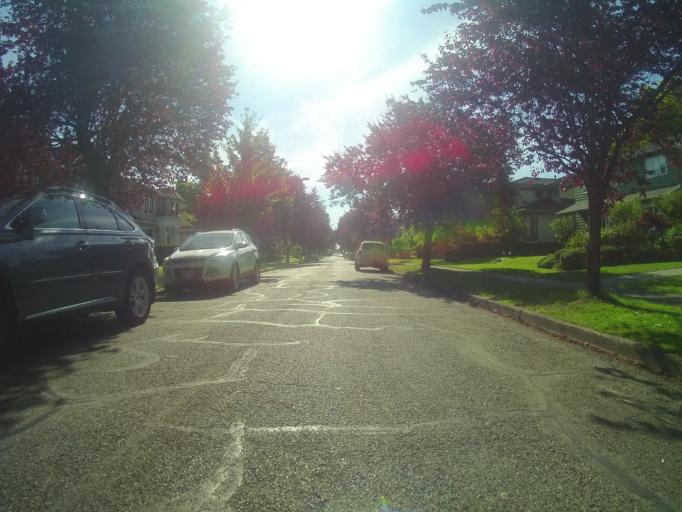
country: CA
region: British Columbia
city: Vancouver
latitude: 49.2177
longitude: -123.1449
